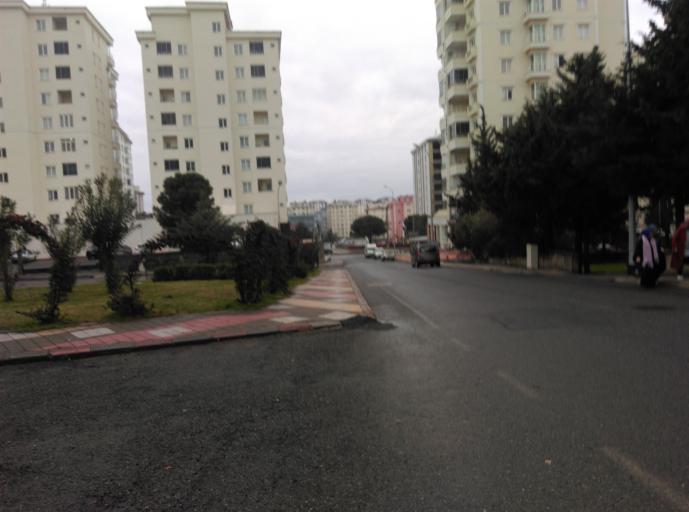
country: TR
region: Kahramanmaras
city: Kahramanmaras
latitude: 37.5853
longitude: 36.8935
